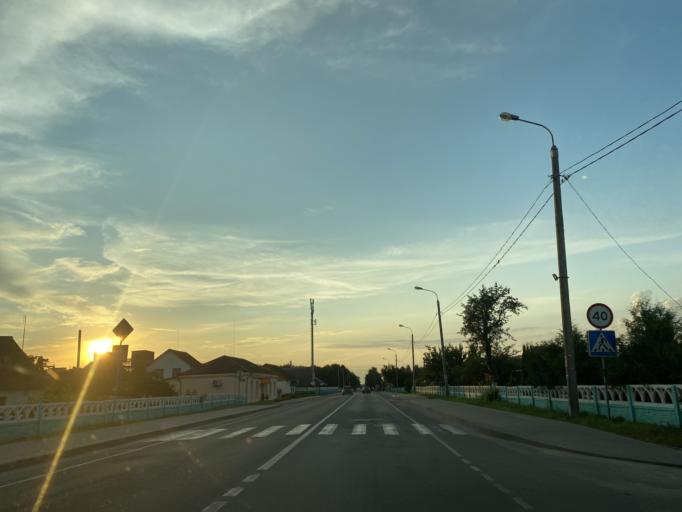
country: BY
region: Brest
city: Ivatsevichy
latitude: 52.7103
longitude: 25.3528
